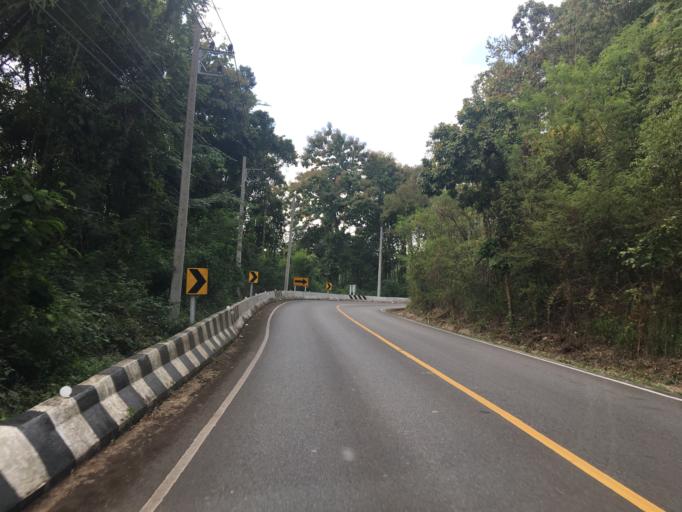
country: TH
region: Nan
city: Nan
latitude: 18.8659
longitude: 100.6306
